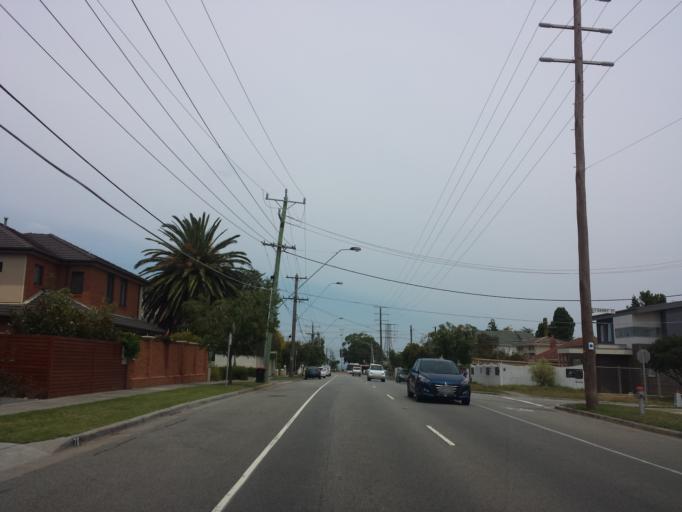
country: AU
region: Victoria
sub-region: Kingston
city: Mentone
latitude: -37.9861
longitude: 145.0706
